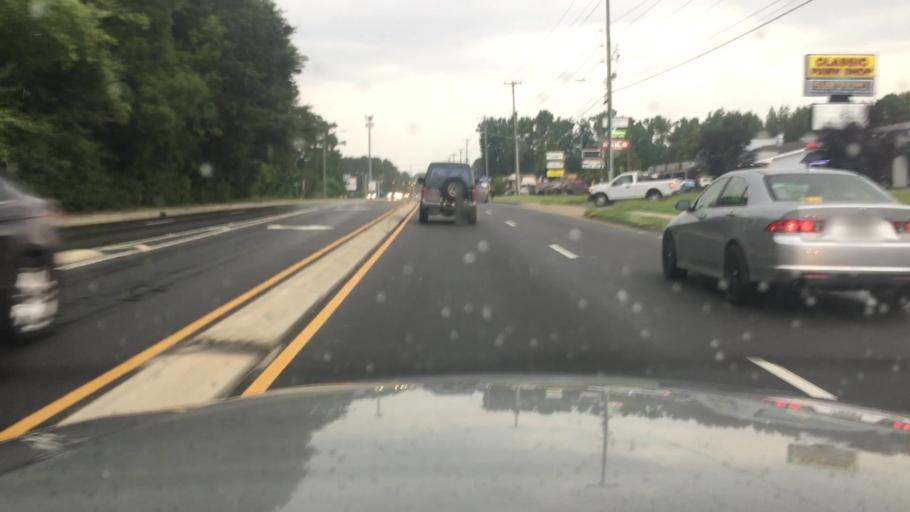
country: US
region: North Carolina
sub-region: Cumberland County
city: Fort Bragg
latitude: 35.0699
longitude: -79.0127
